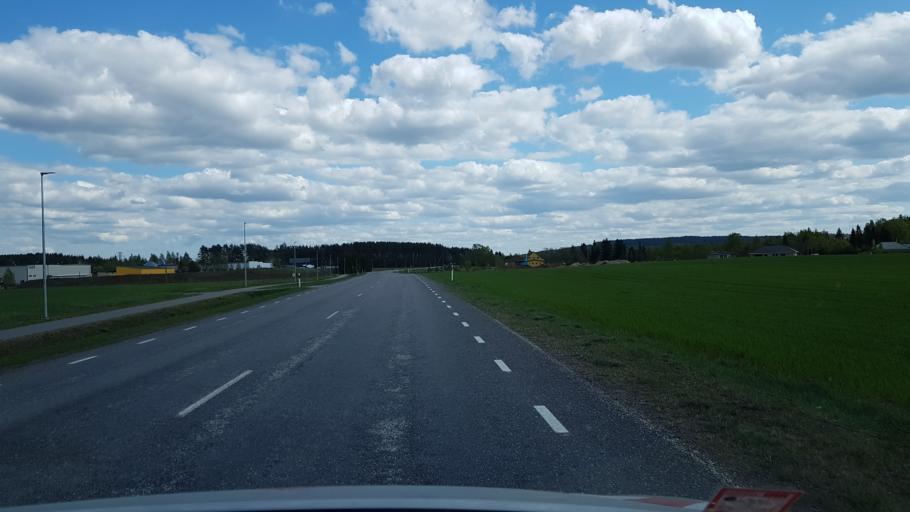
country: EE
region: Tartu
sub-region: UElenurme vald
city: Ulenurme
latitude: 58.3071
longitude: 26.8541
